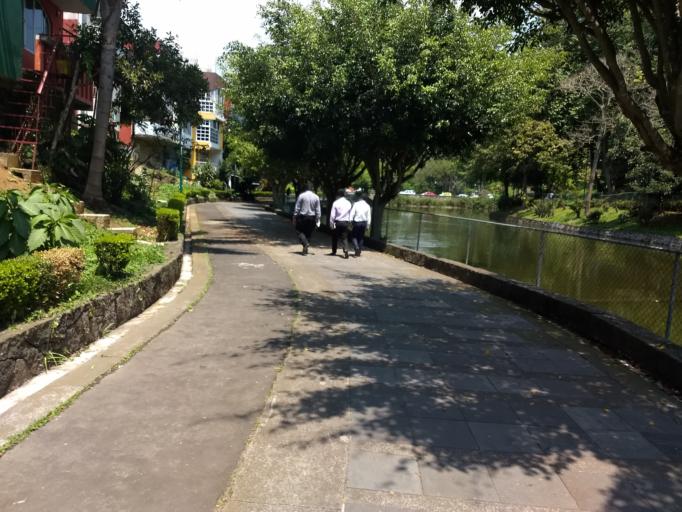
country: MX
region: Veracruz
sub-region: Xalapa
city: Xalapa de Enriquez
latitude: 19.5166
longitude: -96.9201
